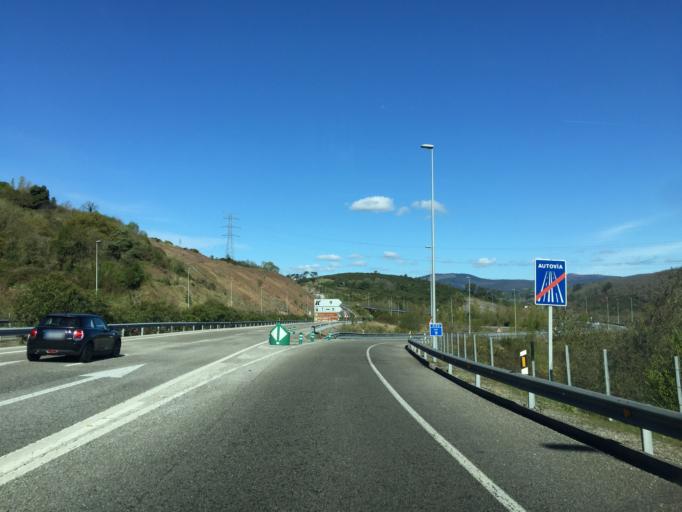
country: ES
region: Asturias
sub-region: Province of Asturias
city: Llanera
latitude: 43.3608
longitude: -5.9469
